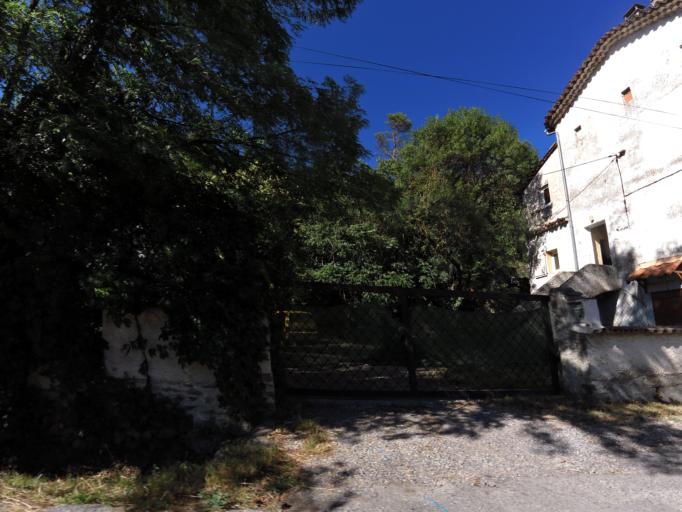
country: FR
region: Languedoc-Roussillon
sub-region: Departement du Gard
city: Saint-Jean-du-Gard
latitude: 44.0996
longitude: 3.8981
